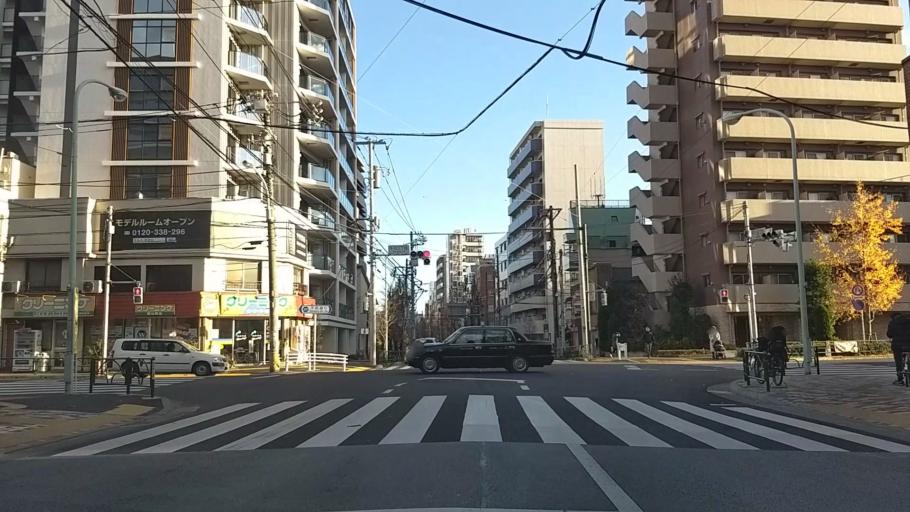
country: JP
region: Tokyo
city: Tokyo
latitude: 35.7237
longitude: 139.7371
